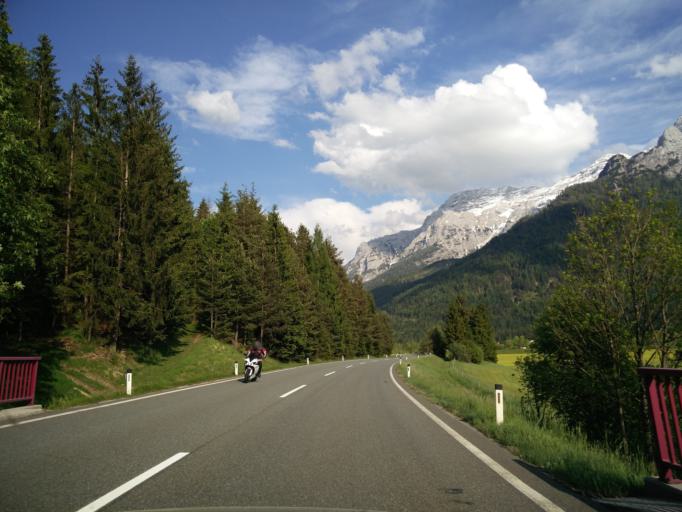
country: AT
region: Tyrol
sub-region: Politischer Bezirk Kitzbuhel
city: Waidring
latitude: 47.5870
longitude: 12.5747
